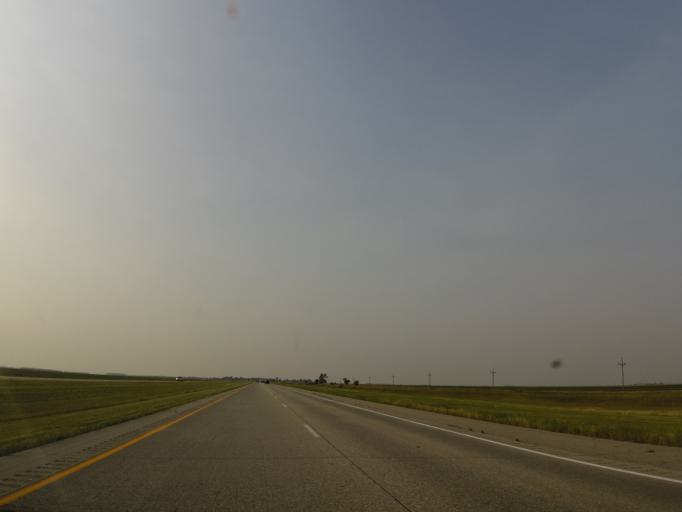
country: US
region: North Dakota
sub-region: Cass County
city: West Fargo
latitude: 47.0306
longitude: -96.9185
